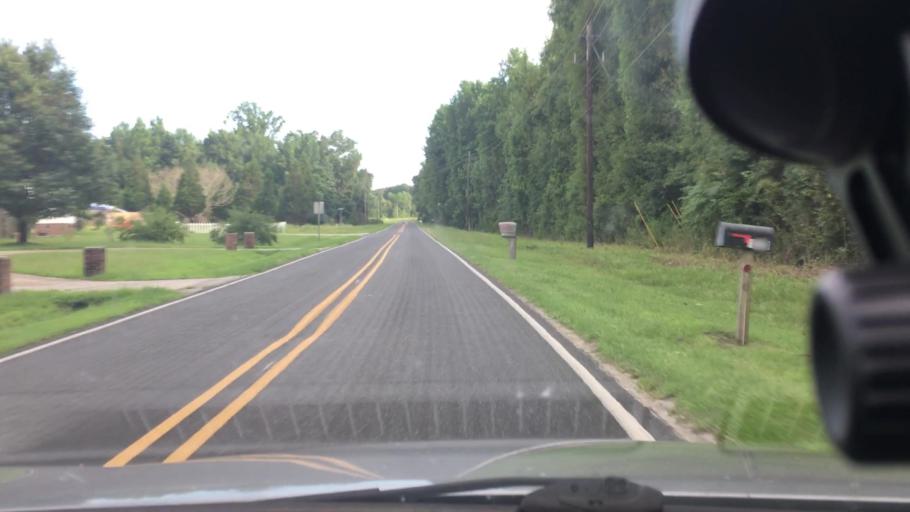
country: US
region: North Carolina
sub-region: Craven County
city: New Bern
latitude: 35.1882
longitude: -77.0584
